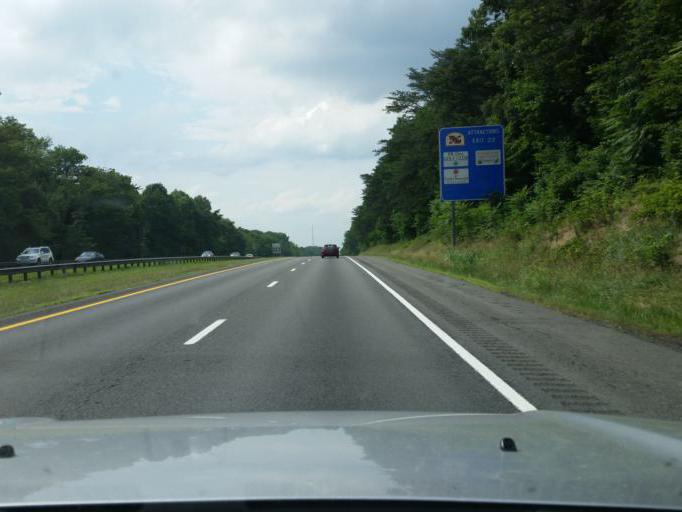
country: US
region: Maryland
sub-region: Montgomery County
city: Clarksburg
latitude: 39.2414
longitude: -77.2931
